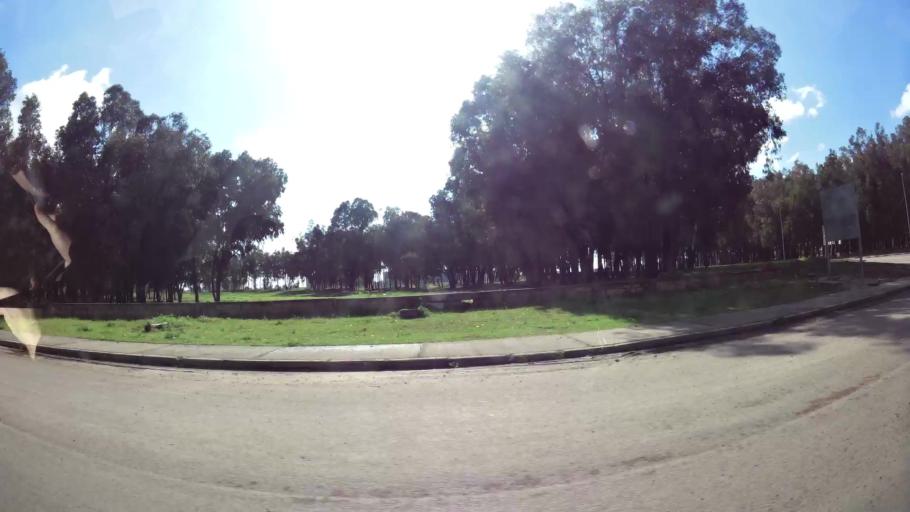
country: MA
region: Grand Casablanca
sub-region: Mediouna
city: Mediouna
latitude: 33.3940
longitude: -7.5531
